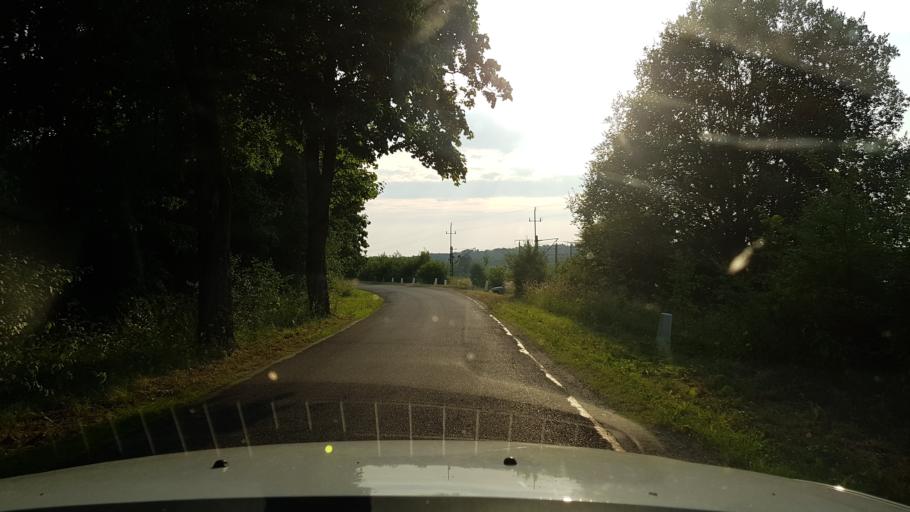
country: PL
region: West Pomeranian Voivodeship
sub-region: Powiat swidwinski
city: Swidwin
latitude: 53.8096
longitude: 15.8032
